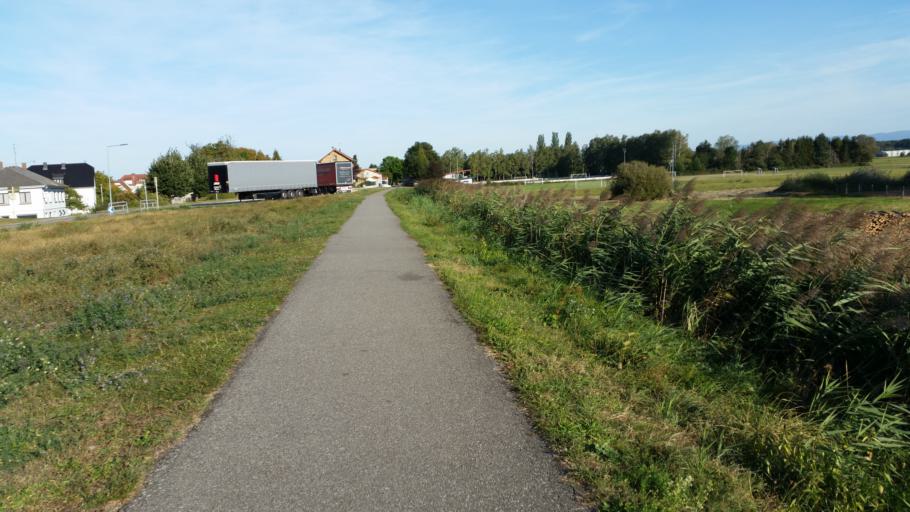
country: FR
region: Alsace
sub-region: Departement du Bas-Rhin
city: Betschdorf
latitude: 48.8962
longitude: 7.9043
